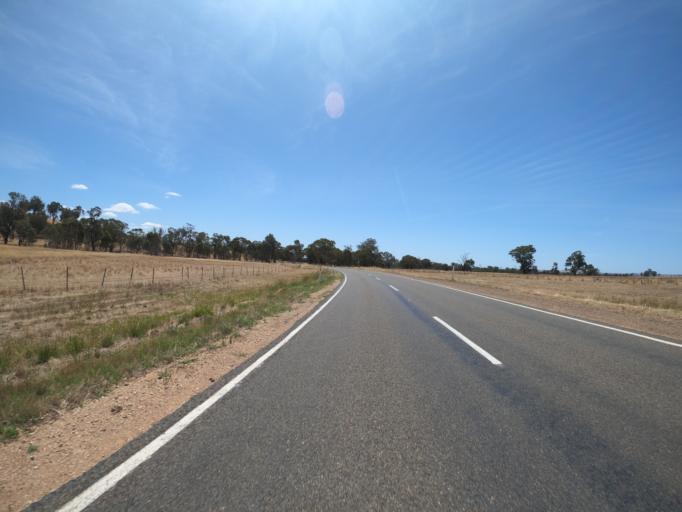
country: AU
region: Victoria
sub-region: Benalla
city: Benalla
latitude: -36.3300
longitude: 145.9615
